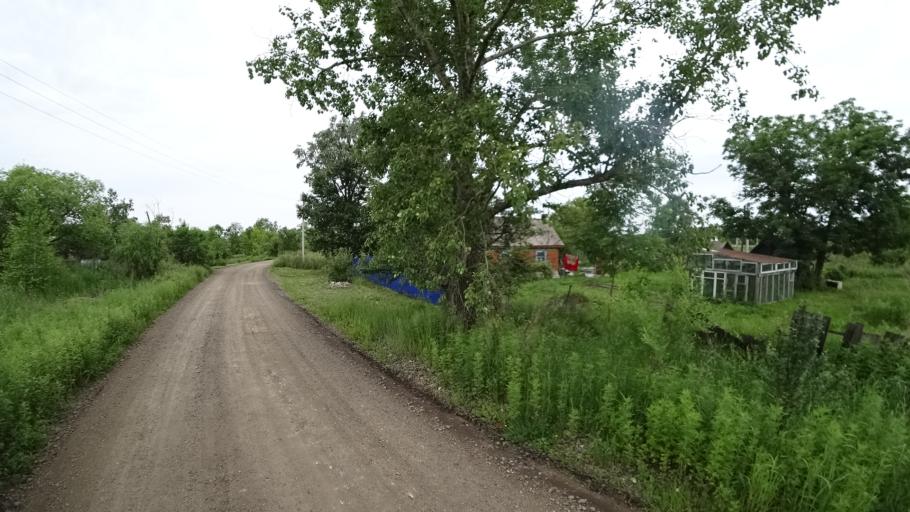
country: RU
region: Primorskiy
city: Novosysoyevka
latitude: 44.2103
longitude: 133.3392
